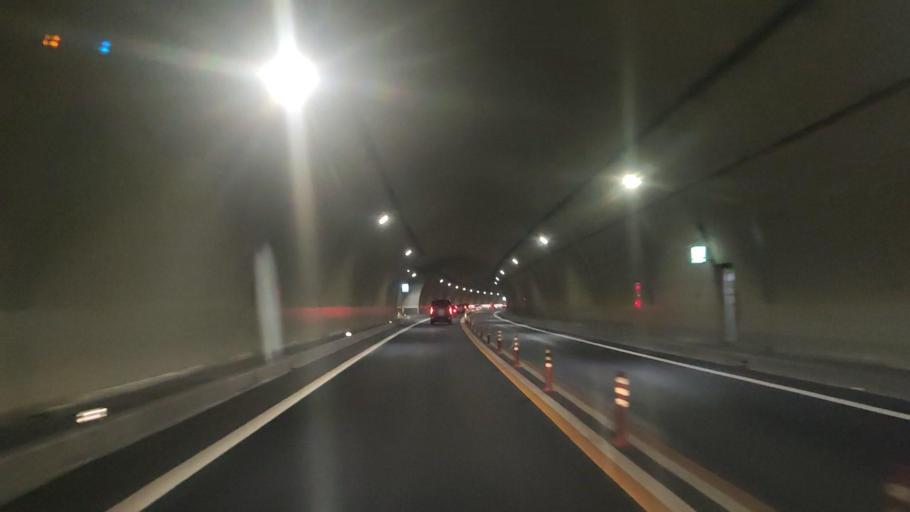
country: JP
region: Fukuoka
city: Nakatsu
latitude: 33.5191
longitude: 131.2612
